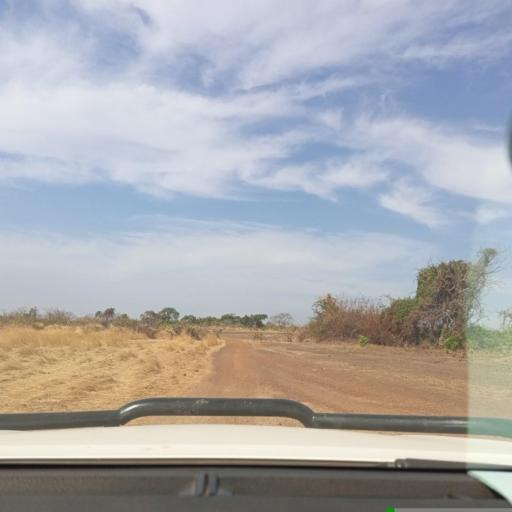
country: ML
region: Koulikoro
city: Kati
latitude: 12.7426
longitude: -8.2487
